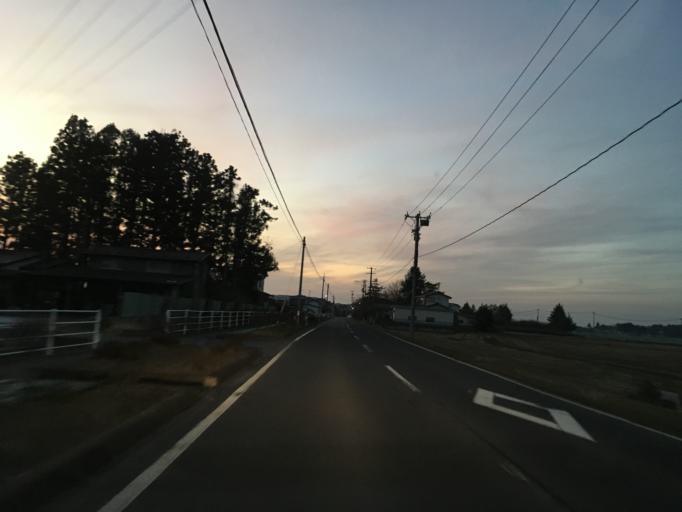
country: JP
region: Miyagi
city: Wakuya
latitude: 38.7129
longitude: 141.2239
